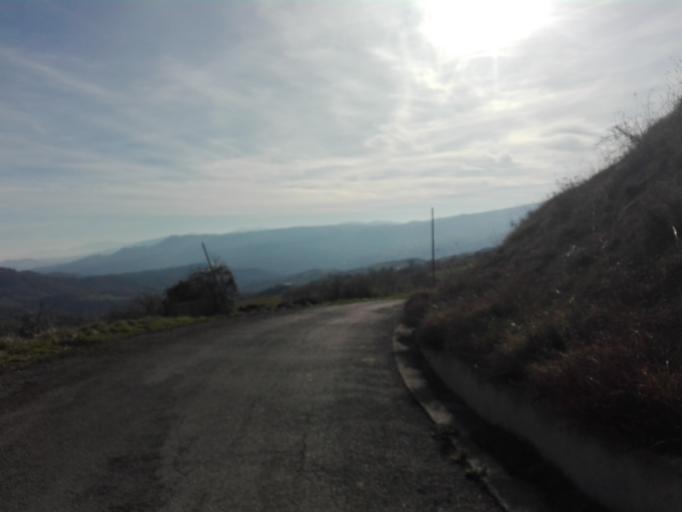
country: IT
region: Molise
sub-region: Provincia di Isernia
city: Agnone
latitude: 41.8536
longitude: 14.3567
